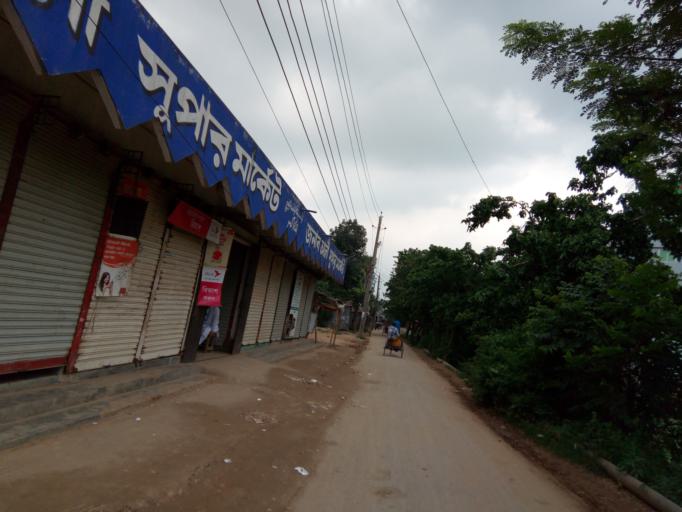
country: BD
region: Dhaka
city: Paltan
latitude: 23.7545
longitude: 90.4543
